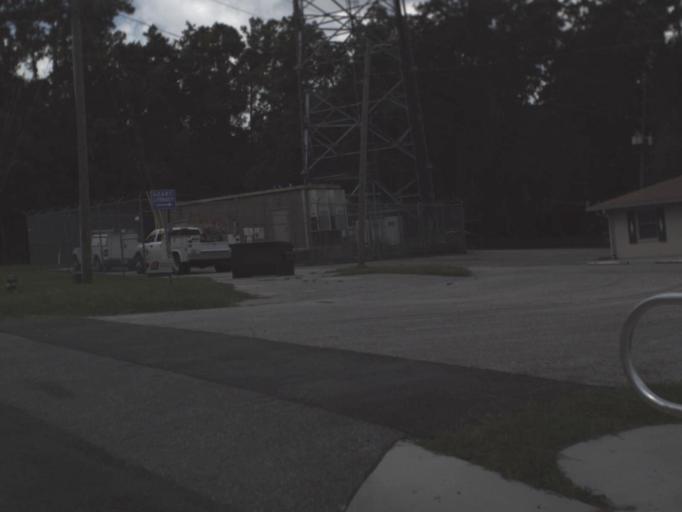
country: US
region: Florida
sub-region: Hernando County
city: Brooksville
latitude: 28.5636
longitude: -82.3758
